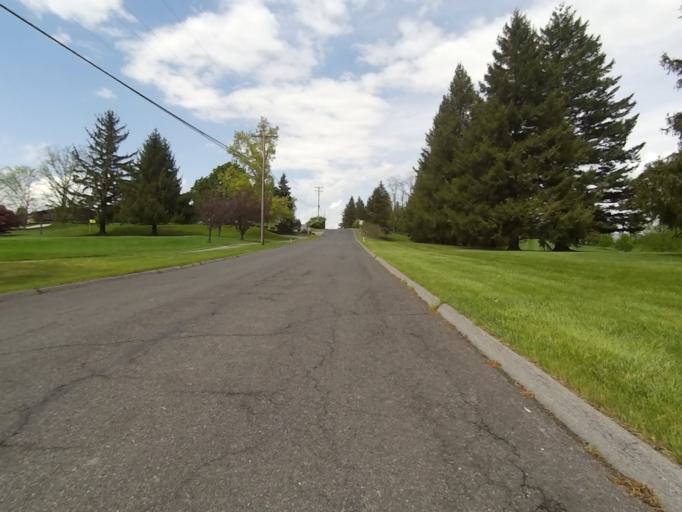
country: US
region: Pennsylvania
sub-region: Centre County
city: Boalsburg
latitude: 40.7833
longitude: -77.7592
